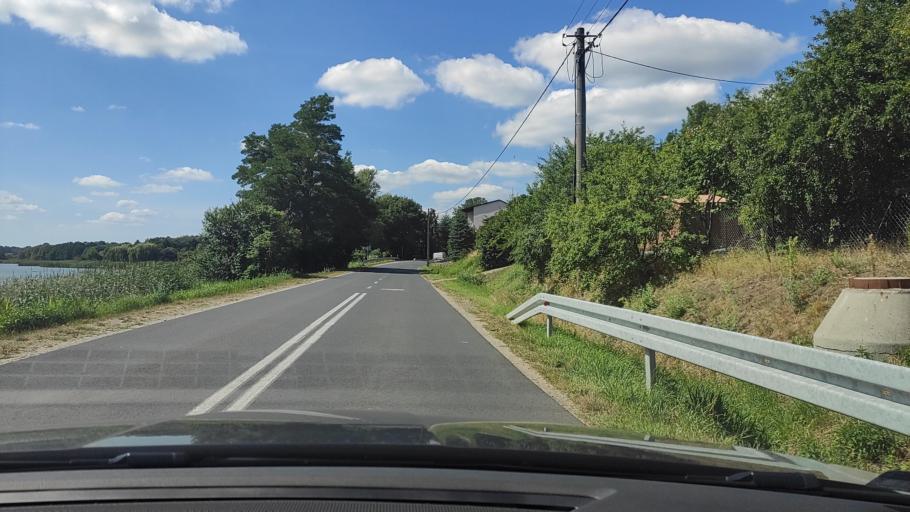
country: PL
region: Greater Poland Voivodeship
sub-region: Powiat poznanski
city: Kostrzyn
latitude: 52.4778
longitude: 17.1806
